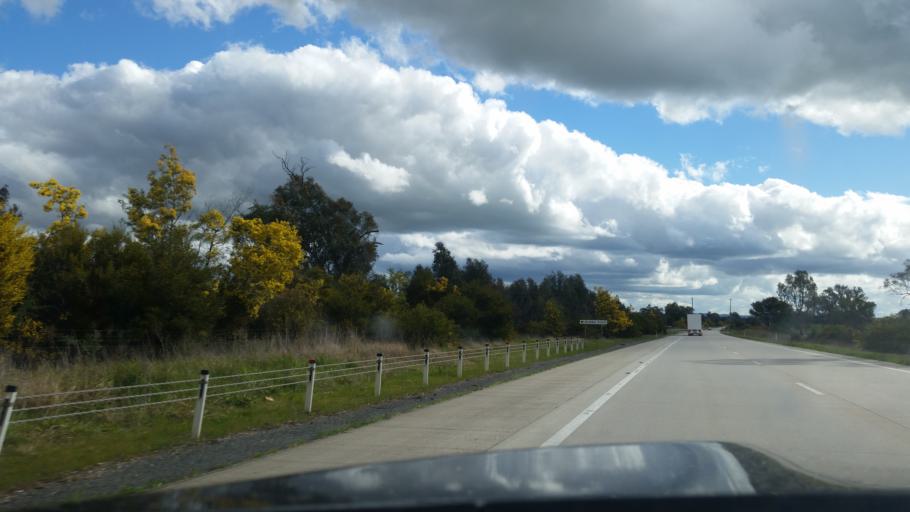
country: AU
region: New South Wales
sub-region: Greater Hume Shire
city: Jindera
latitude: -35.9252
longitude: 147.0369
